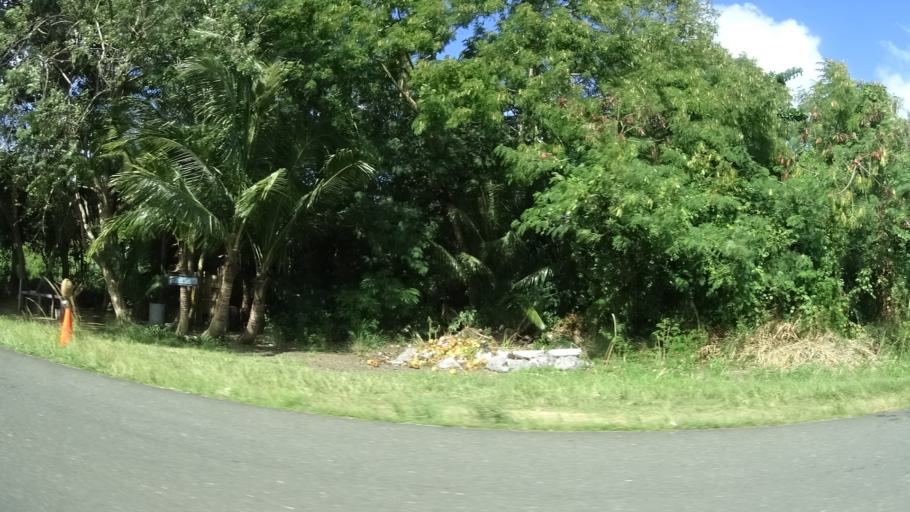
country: PR
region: Luquillo
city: Playa Fortuna
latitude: 18.3796
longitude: -65.7478
